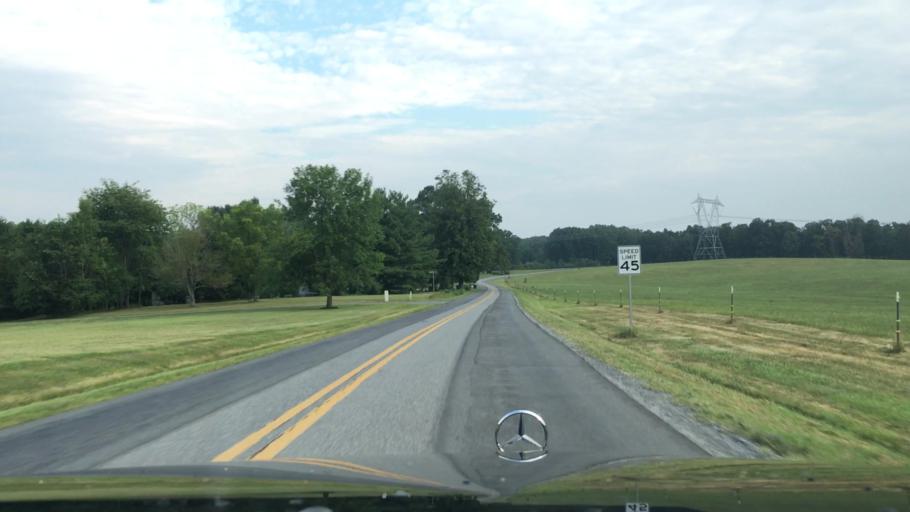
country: US
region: Virginia
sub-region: Campbell County
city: Timberlake
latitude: 37.2792
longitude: -79.3170
